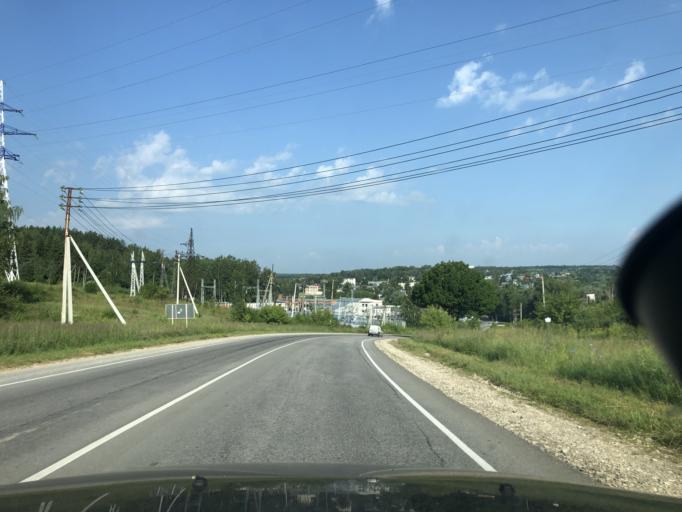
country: RU
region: Tula
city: Dubna
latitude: 54.1473
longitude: 36.9742
